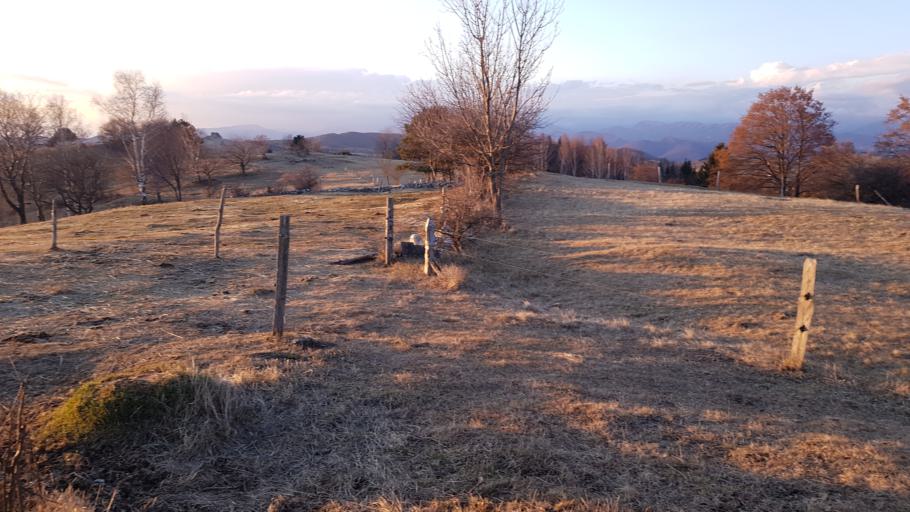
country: SI
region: Nova Gorica
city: Kromberk
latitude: 46.0330
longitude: 13.7166
